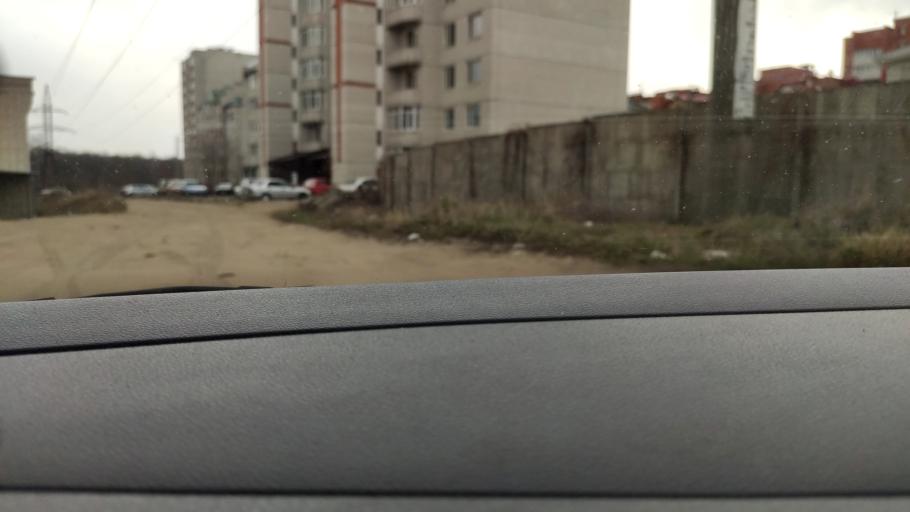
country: RU
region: Voronezj
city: Podgornoye
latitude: 51.7347
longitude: 39.1933
